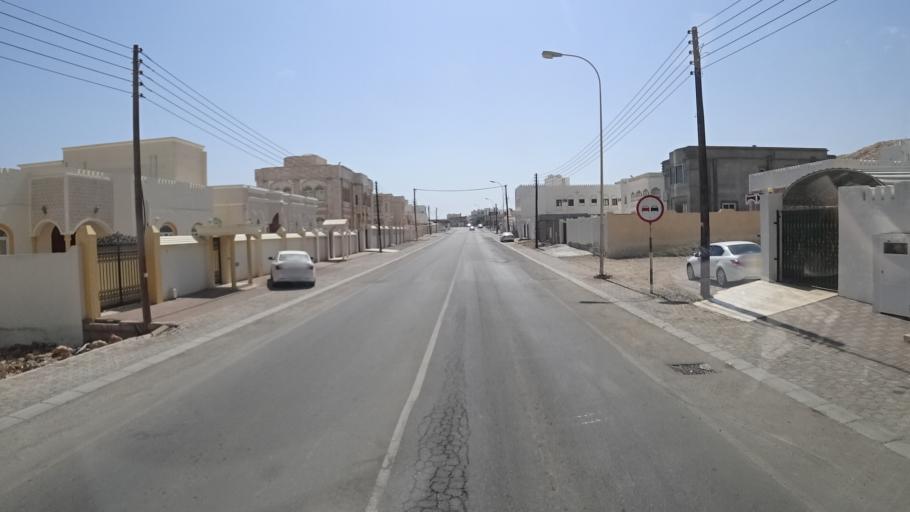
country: OM
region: Ash Sharqiyah
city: Sur
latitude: 22.5669
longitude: 59.5502
